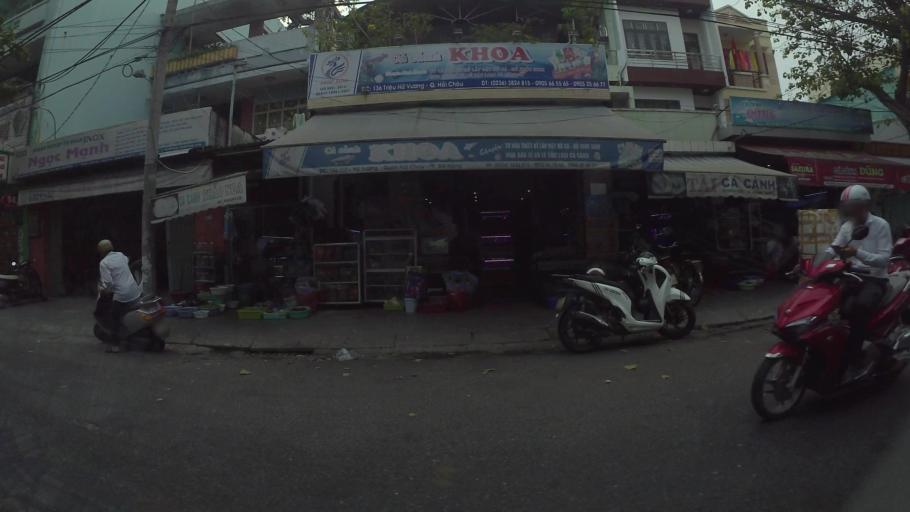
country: VN
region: Da Nang
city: Da Nang
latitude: 16.0631
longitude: 108.2167
